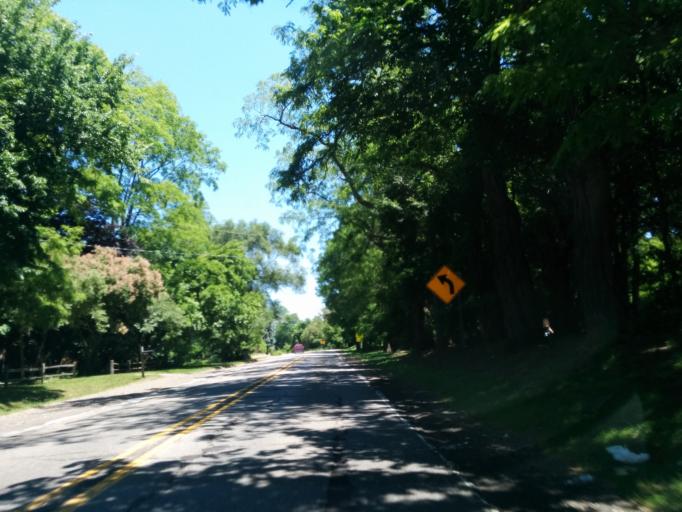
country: US
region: Michigan
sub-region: Oakland County
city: West Bloomfield Township
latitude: 42.5887
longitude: -83.4041
